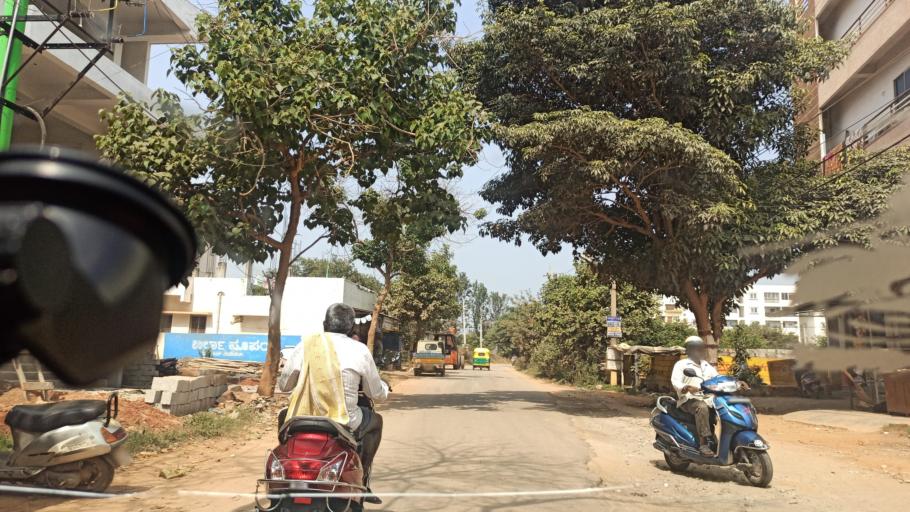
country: IN
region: Karnataka
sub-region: Bangalore Urban
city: Yelahanka
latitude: 13.0946
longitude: 77.6186
